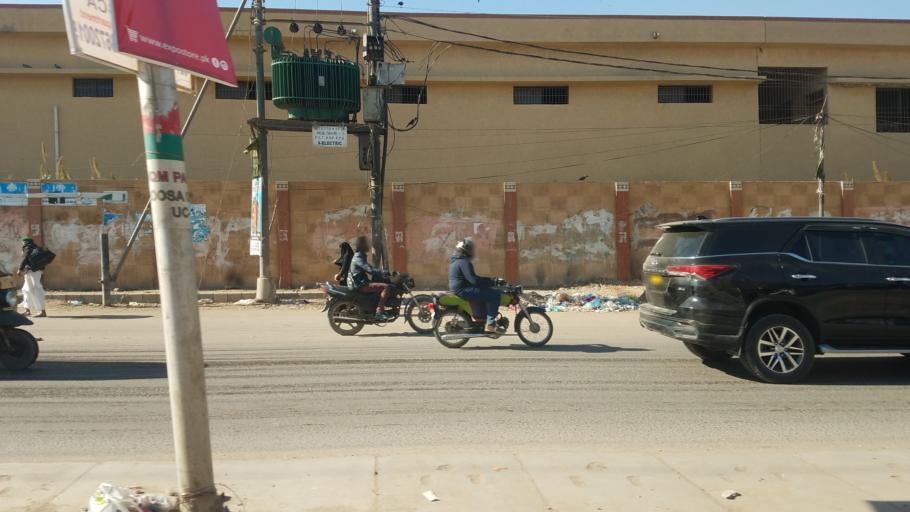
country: PK
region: Sindh
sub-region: Karachi District
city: Karachi
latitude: 24.9202
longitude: 67.0518
